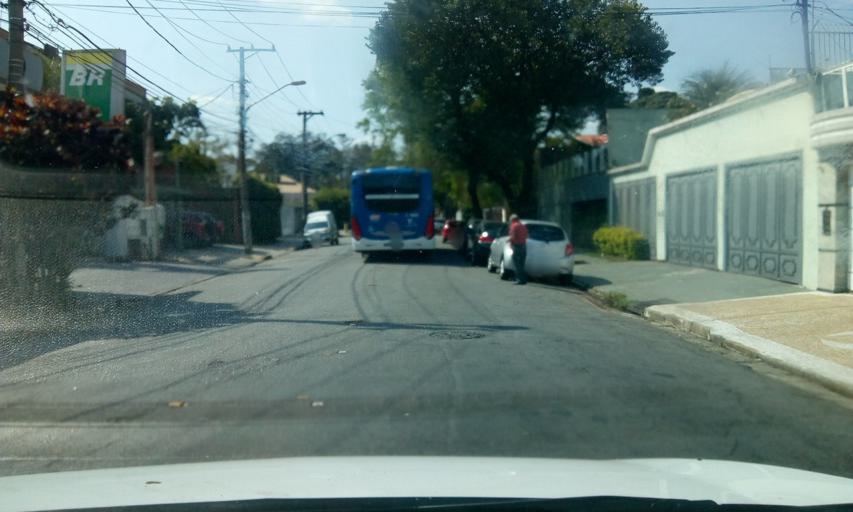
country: BR
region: Sao Paulo
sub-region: Osasco
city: Osasco
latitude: -23.5283
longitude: -46.7248
